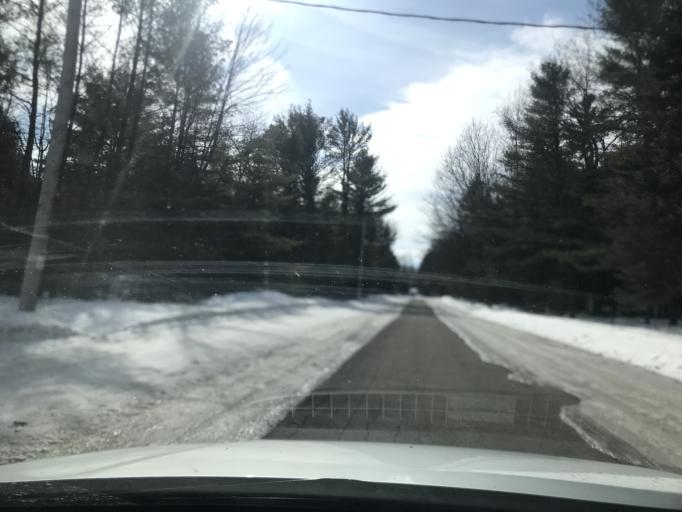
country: US
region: Wisconsin
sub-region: Menominee County
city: Legend Lake
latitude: 45.1079
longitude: -88.4330
